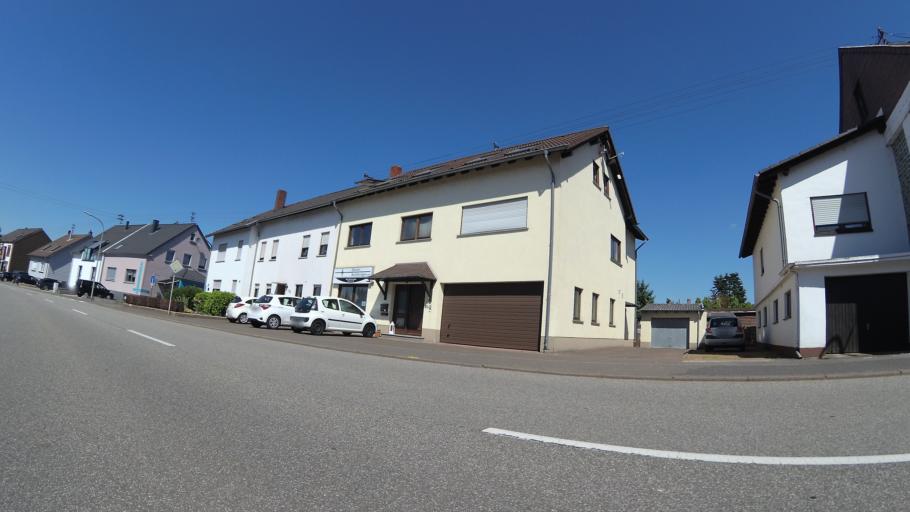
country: DE
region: Saarland
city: Saarwellingen
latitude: 49.3466
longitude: 6.8105
